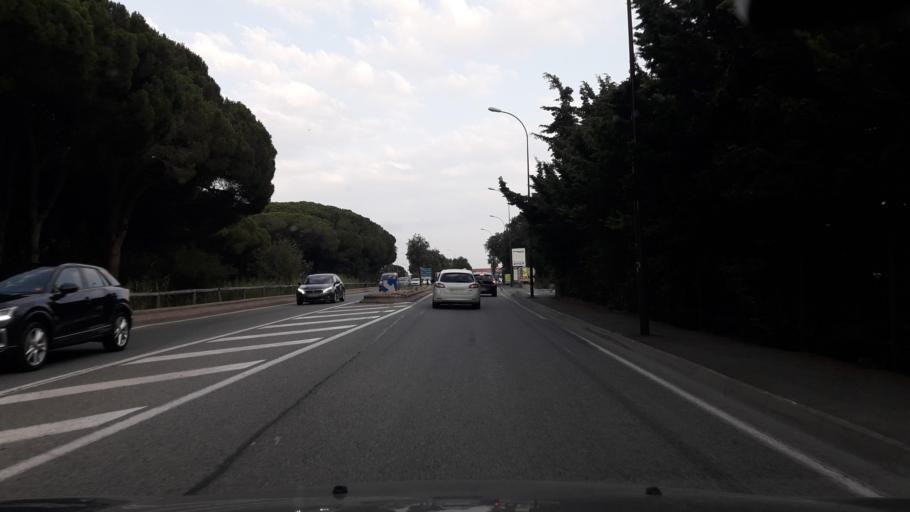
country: FR
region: Provence-Alpes-Cote d'Azur
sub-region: Departement du Var
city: Frejus
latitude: 43.4412
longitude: 6.7427
